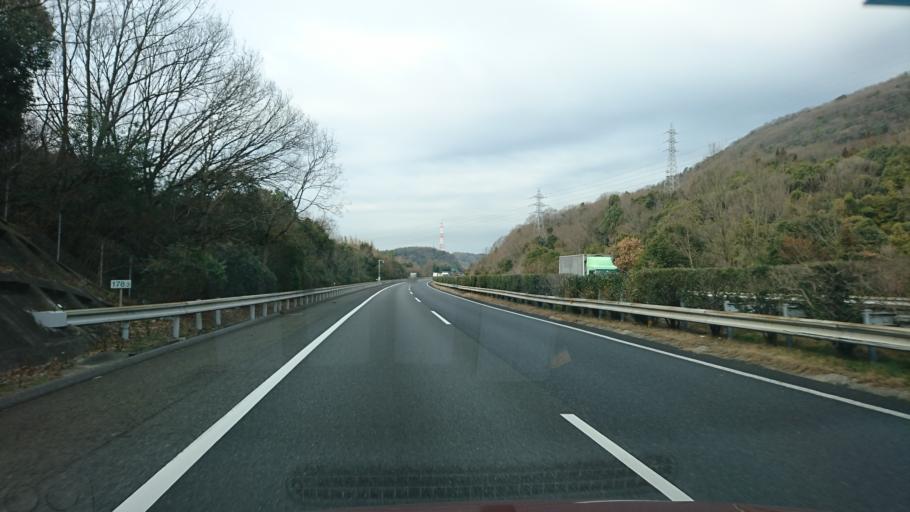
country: JP
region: Okayama
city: Kasaoka
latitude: 34.5319
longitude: 133.5312
